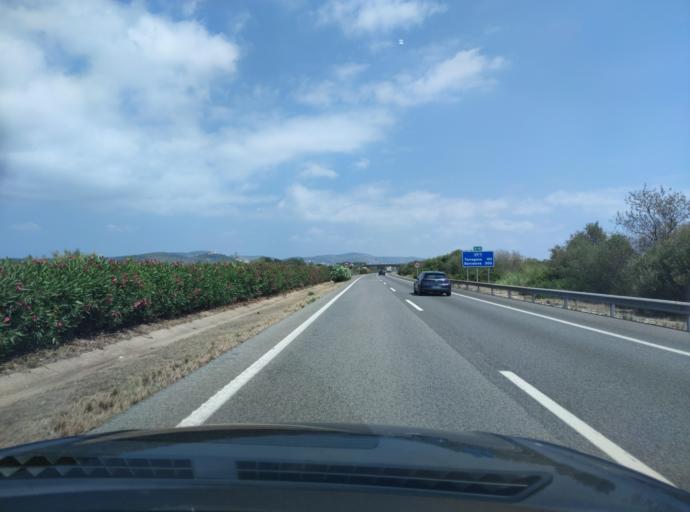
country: ES
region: Catalonia
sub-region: Provincia de Tarragona
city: Ulldecona
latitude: 40.5619
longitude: 0.4290
